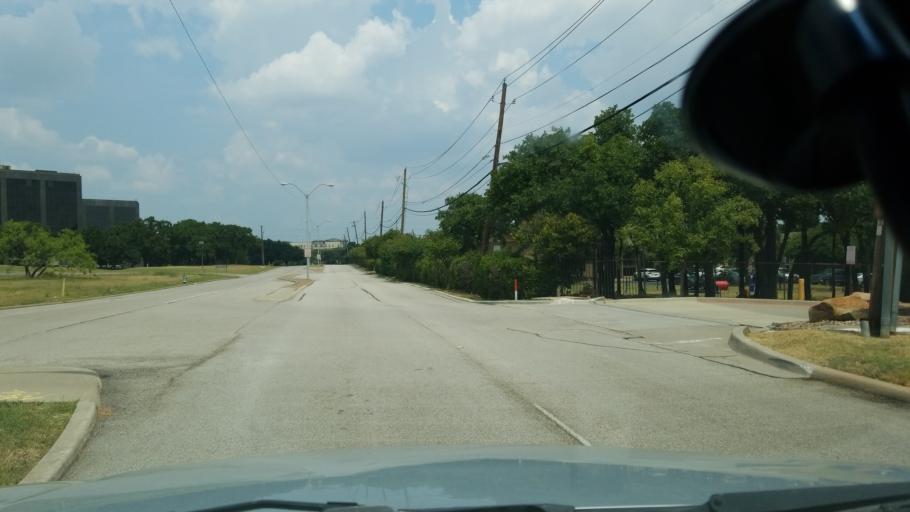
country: US
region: Texas
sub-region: Dallas County
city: Irving
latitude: 32.8403
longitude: -96.9223
